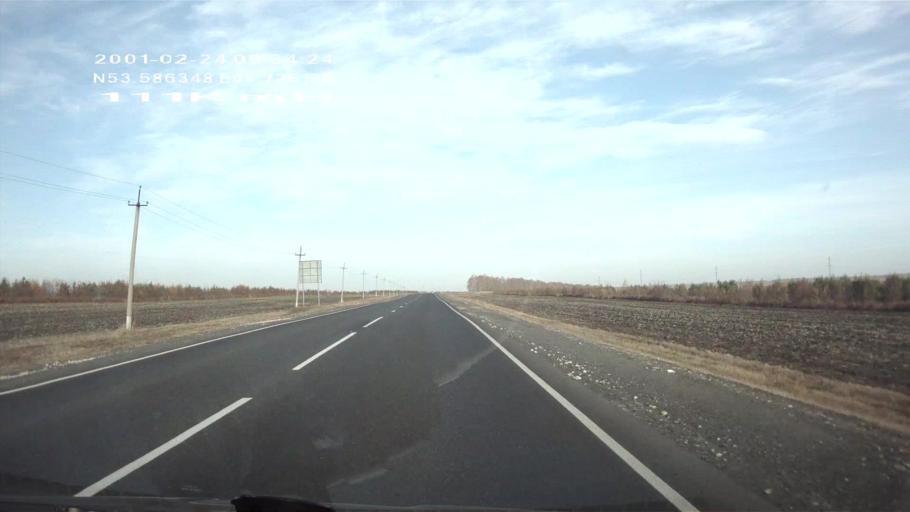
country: RU
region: Penza
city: Mokshan
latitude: 53.5867
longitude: 44.7277
